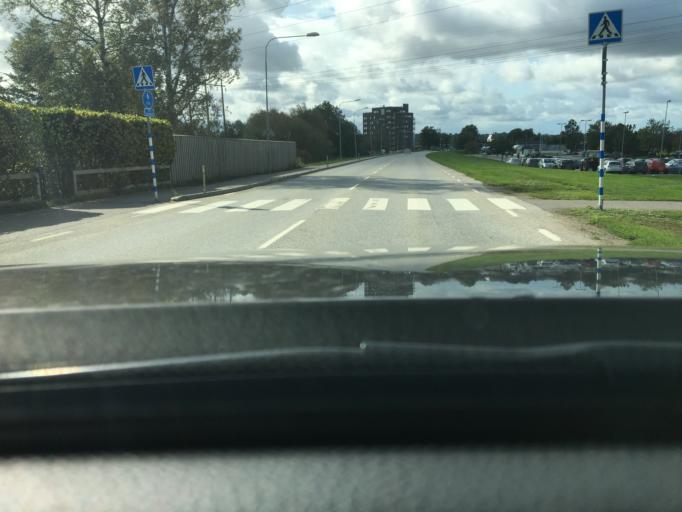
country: SE
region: Skane
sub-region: Horby Kommun
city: Hoerby
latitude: 55.8565
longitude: 13.6740
